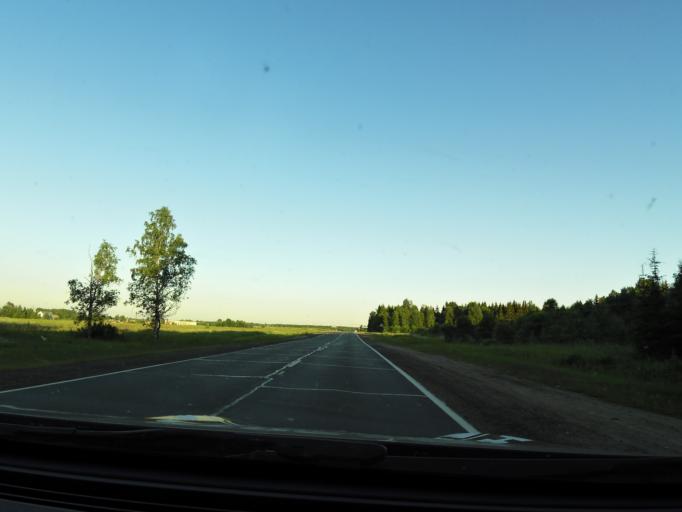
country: RU
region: Vologda
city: Gryazovets
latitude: 58.8042
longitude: 40.2480
